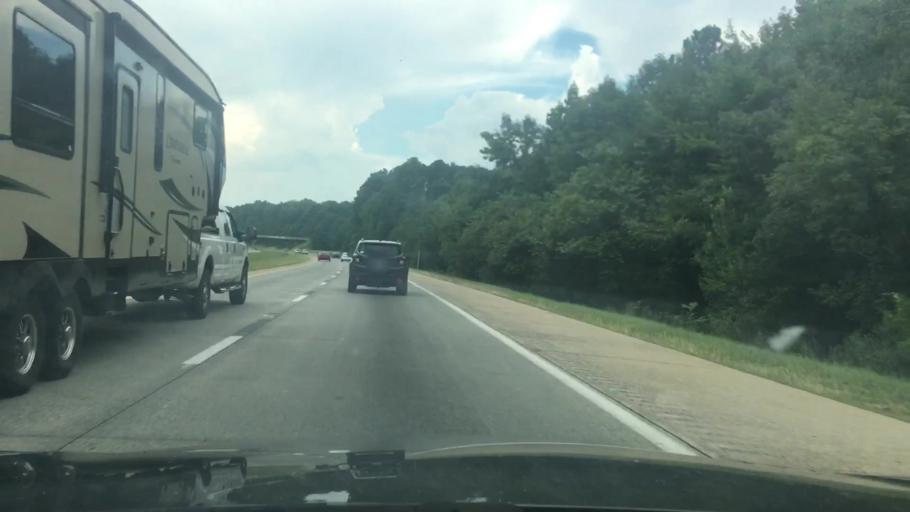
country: US
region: North Carolina
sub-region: Orange County
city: Chapel Hill
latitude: 35.9687
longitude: -79.0283
